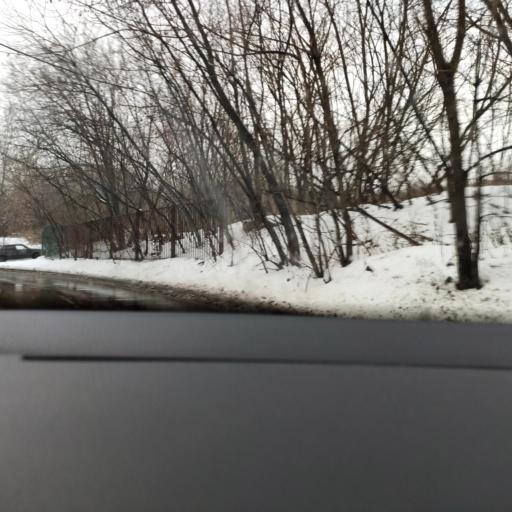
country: RU
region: Moscow
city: Metrogorodok
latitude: 55.8246
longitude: 37.7793
